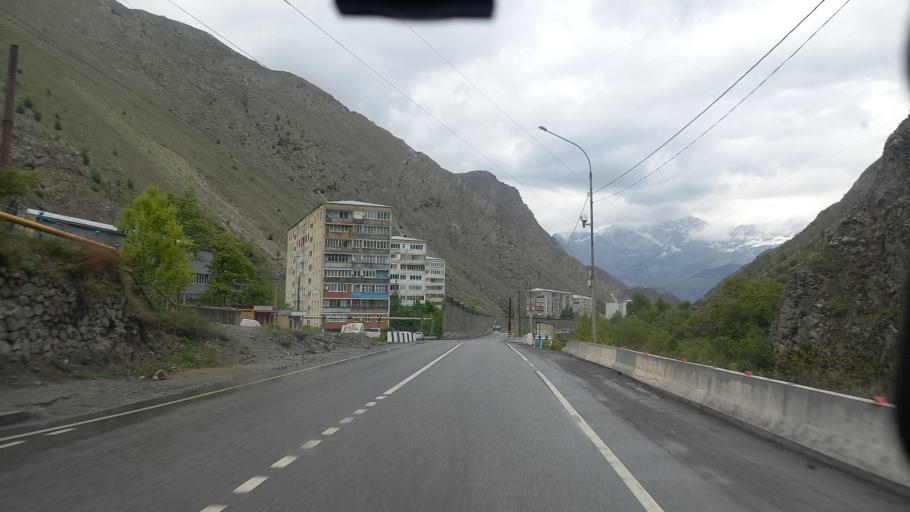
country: RU
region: North Ossetia
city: Mizur
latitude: 42.8506
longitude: 44.0594
